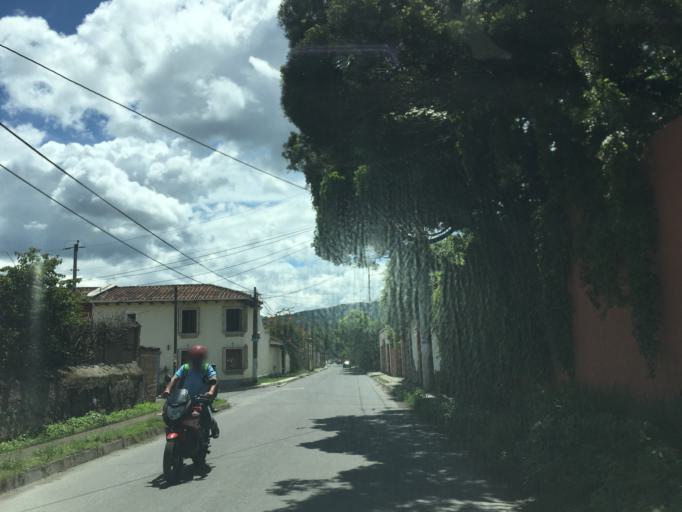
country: GT
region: Sacatepequez
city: Antigua Guatemala
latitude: 14.5436
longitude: -90.7407
